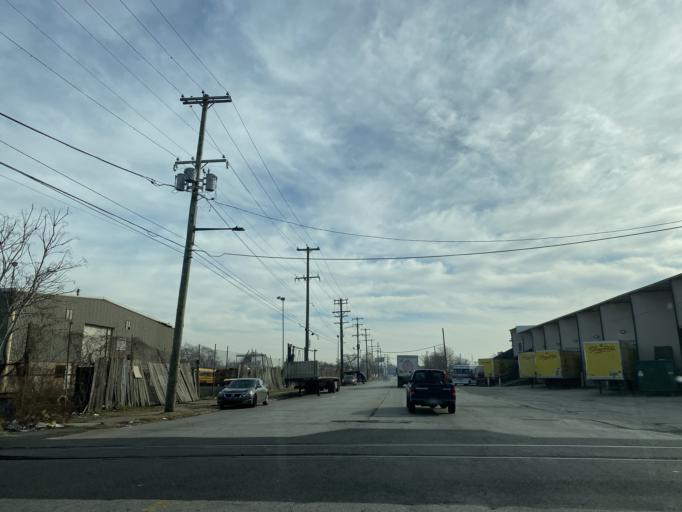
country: US
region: New Jersey
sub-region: Camden County
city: Pennsauken
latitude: 39.9954
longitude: -75.0916
